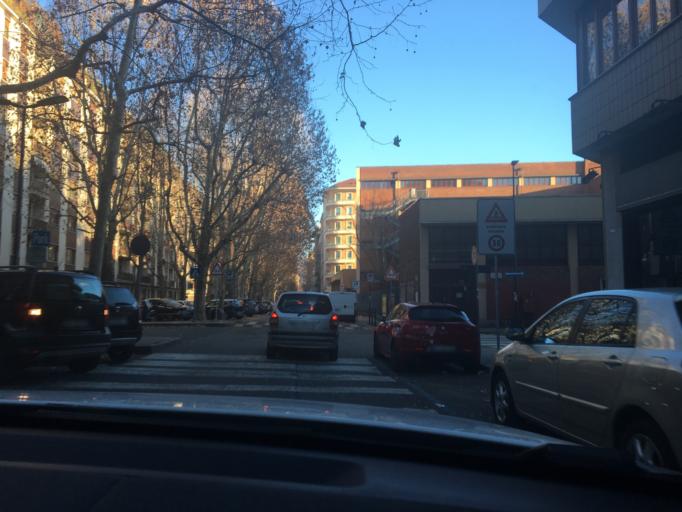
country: IT
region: Piedmont
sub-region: Provincia di Torino
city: Turin
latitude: 45.0525
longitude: 7.6583
